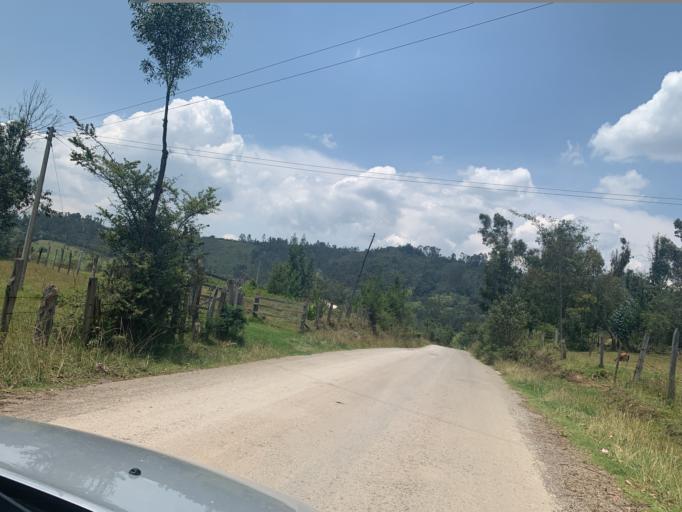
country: CO
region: Boyaca
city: Chiquinquira
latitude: 5.5805
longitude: -73.7488
